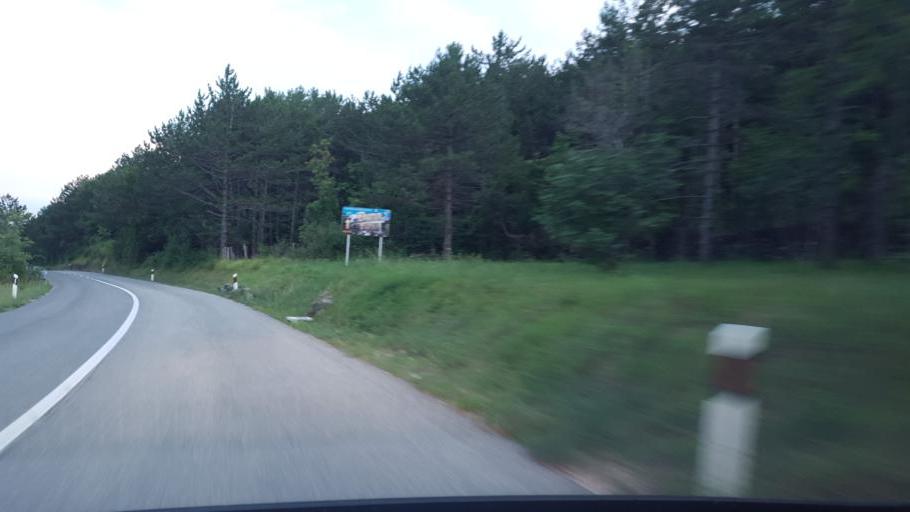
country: HR
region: Primorsko-Goranska
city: Punat
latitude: 45.0064
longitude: 14.7026
